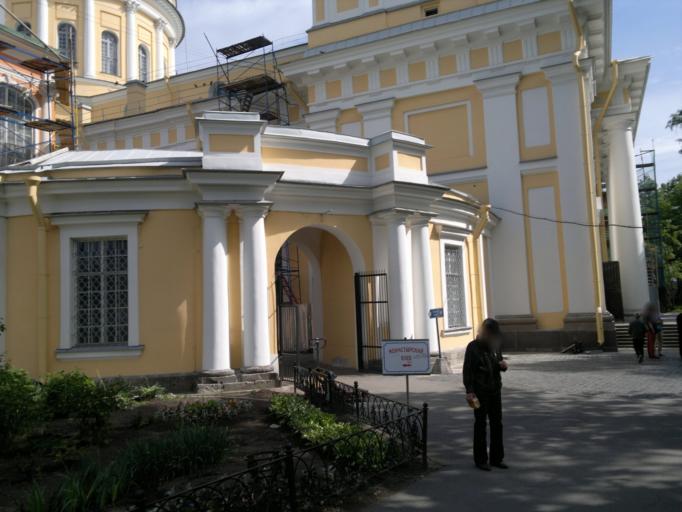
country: RU
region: St.-Petersburg
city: Centralniy
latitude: 59.9213
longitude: 30.3879
